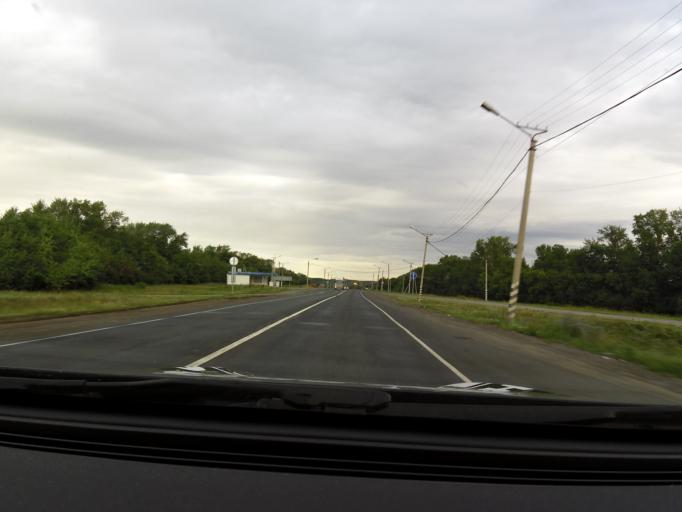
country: RU
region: Chuvashia
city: Kozlovka
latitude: 55.7685
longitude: 48.1956
